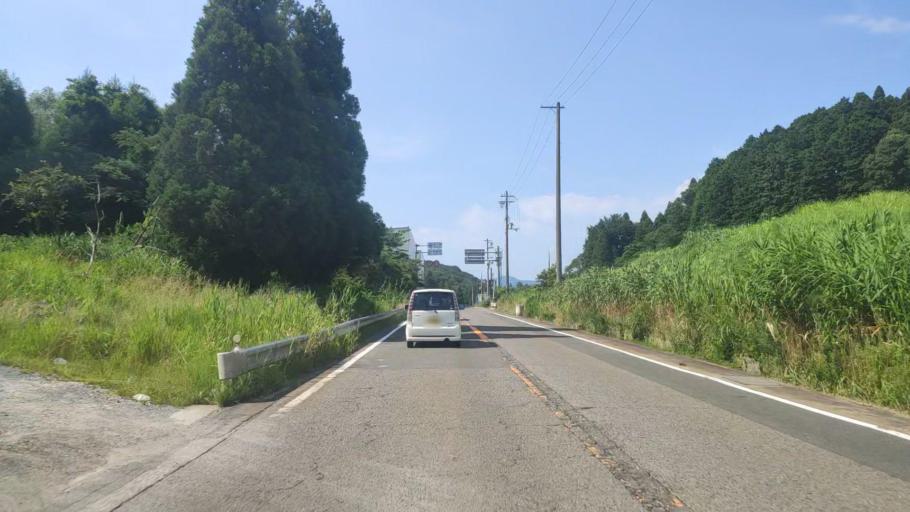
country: JP
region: Fukui
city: Tsuruga
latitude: 35.5754
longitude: 136.1228
